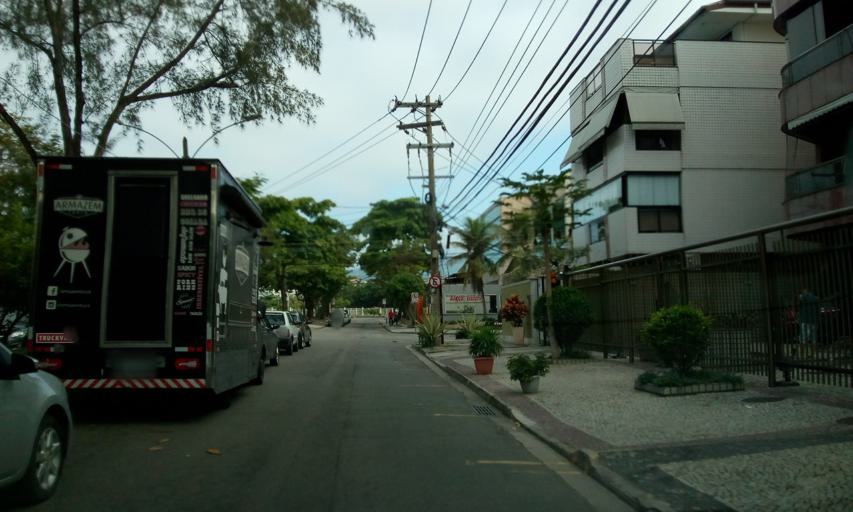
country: BR
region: Rio de Janeiro
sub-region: Nilopolis
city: Nilopolis
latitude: -23.0131
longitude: -43.4558
